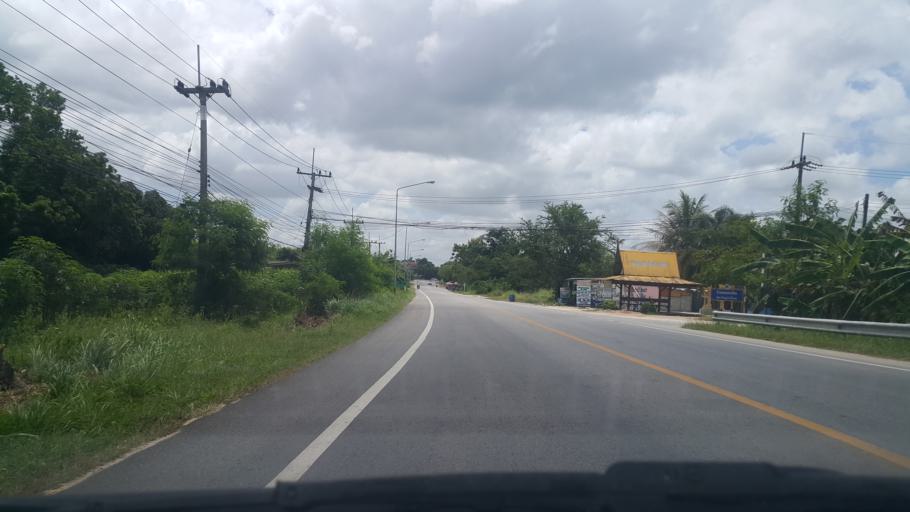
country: TH
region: Rayong
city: Ban Chang
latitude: 12.7879
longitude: 101.0291
